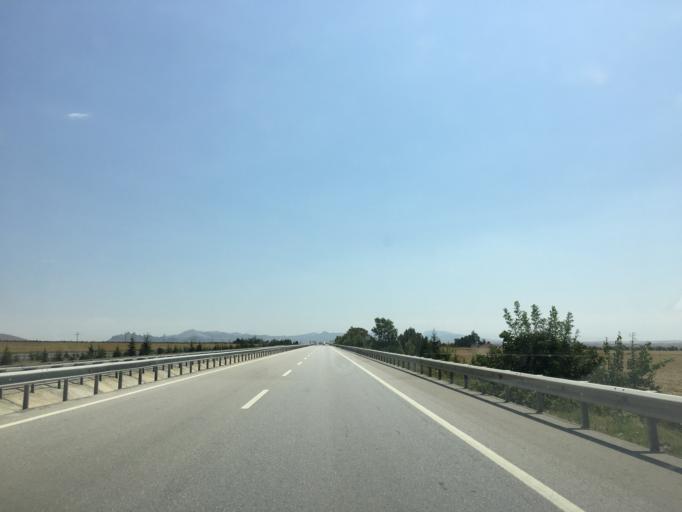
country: TR
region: Eskisehir
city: Sivrihisar
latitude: 39.4597
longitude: 31.3838
